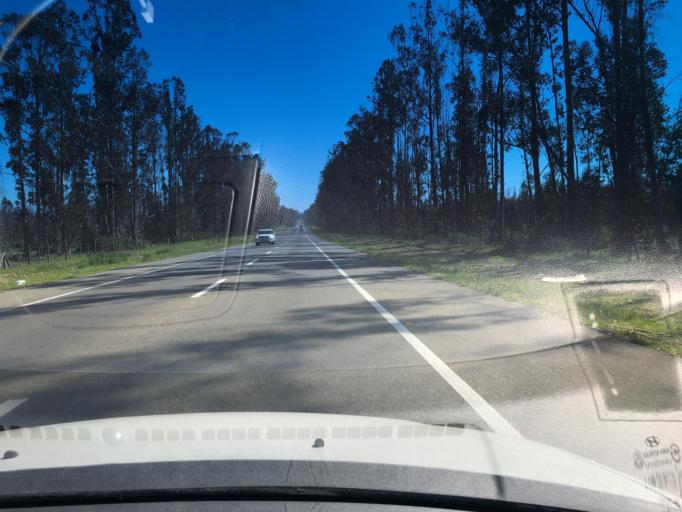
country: CL
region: Valparaiso
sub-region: San Antonio Province
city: El Tabo
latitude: -33.4056
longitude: -71.5649
